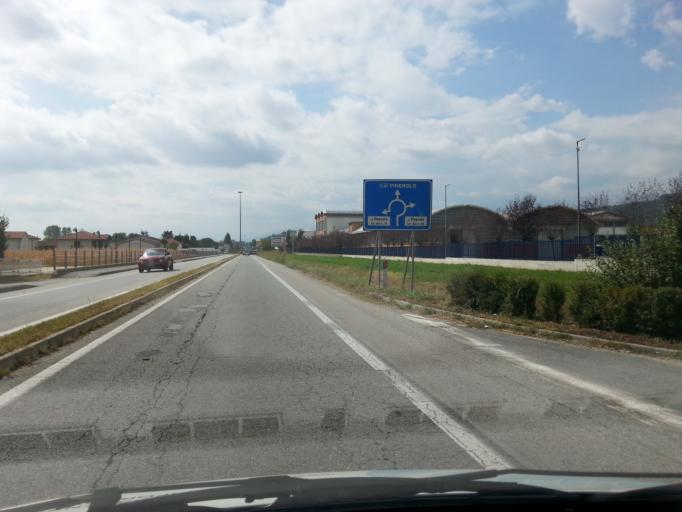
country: IT
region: Piedmont
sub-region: Provincia di Torino
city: Frossasco
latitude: 44.9207
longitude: 7.3658
